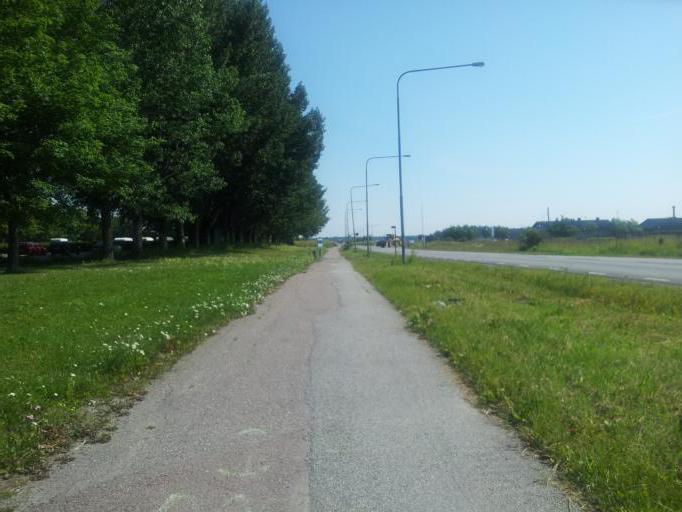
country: SE
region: Uppsala
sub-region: Uppsala Kommun
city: Saevja
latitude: 59.8536
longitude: 17.7073
